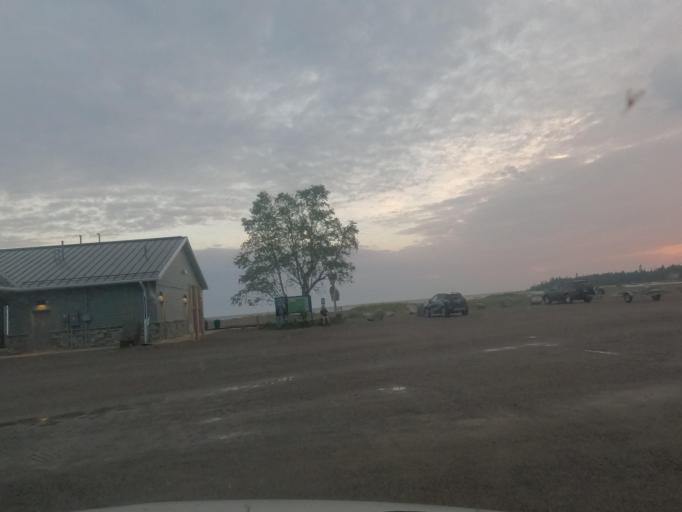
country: CA
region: Ontario
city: Marathon
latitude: 48.7716
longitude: -87.1165
